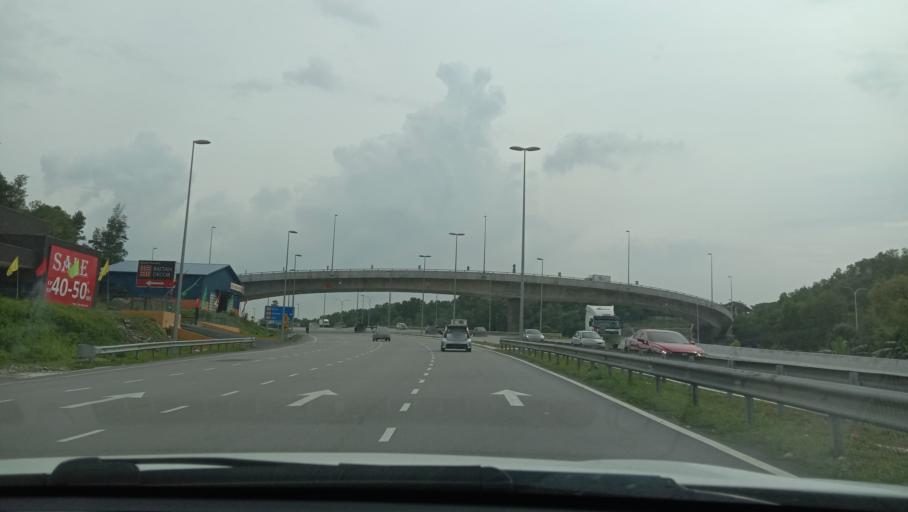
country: MY
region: Selangor
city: Kampung Baru Subang
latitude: 3.1293
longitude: 101.5259
